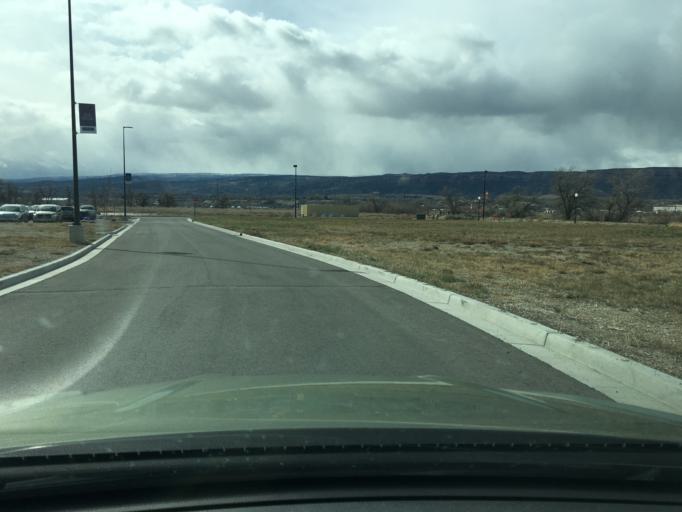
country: US
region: Colorado
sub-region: Mesa County
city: Redlands
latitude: 39.1049
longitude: -108.6165
